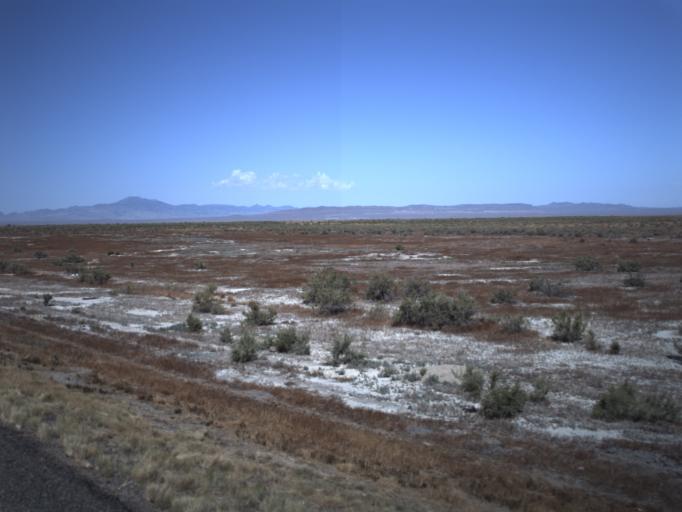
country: US
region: Utah
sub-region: Millard County
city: Delta
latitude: 39.3146
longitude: -112.7547
